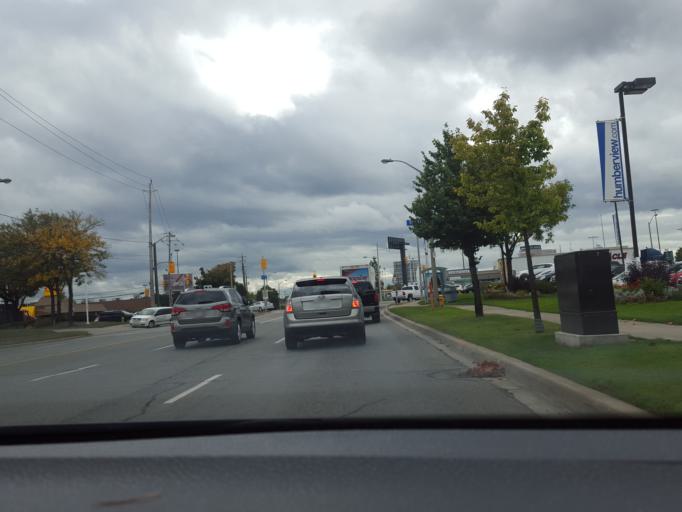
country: CA
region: Ontario
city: Etobicoke
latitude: 43.6173
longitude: -79.5468
